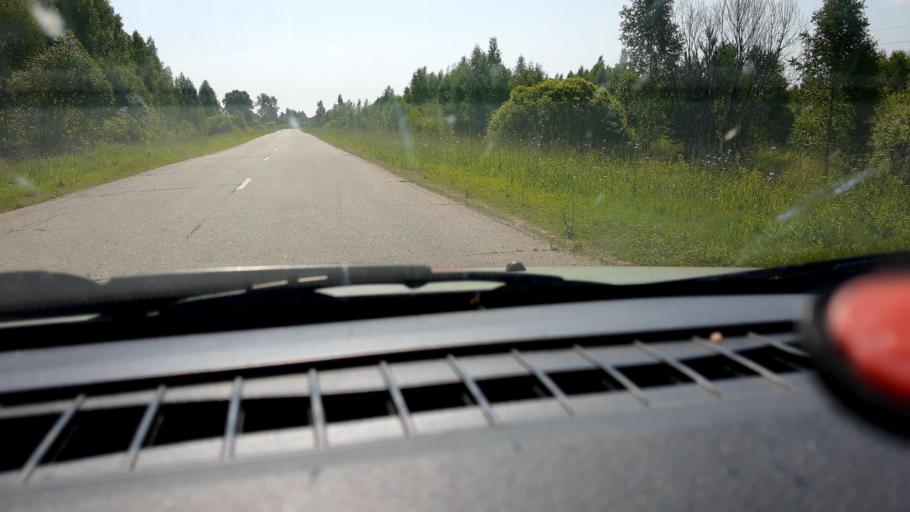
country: RU
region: Nizjnij Novgorod
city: Sharanga
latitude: 57.0330
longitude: 46.5763
